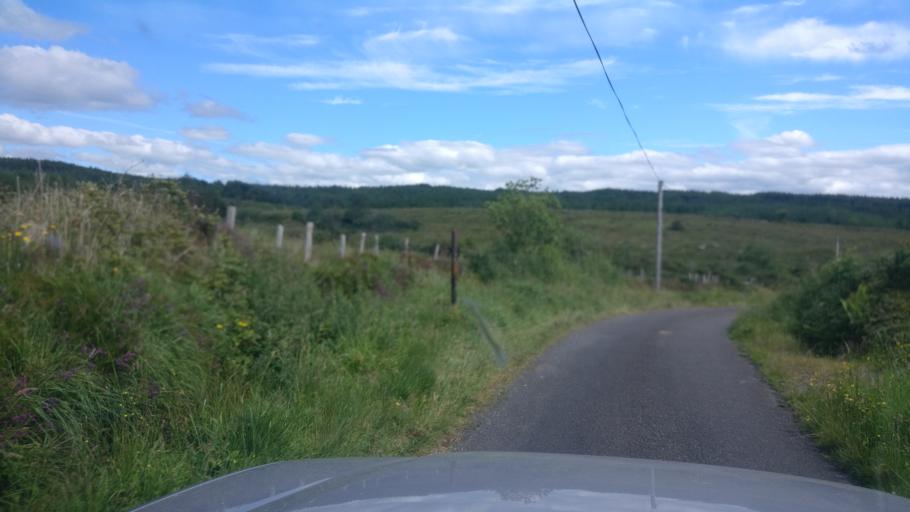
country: IE
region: Connaught
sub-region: County Galway
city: Gort
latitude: 53.0717
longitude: -8.7046
